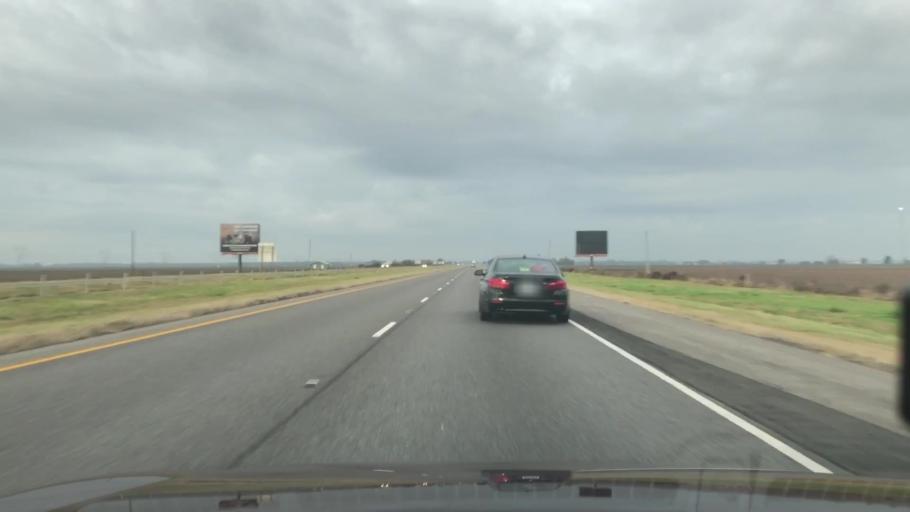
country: US
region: Mississippi
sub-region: Warren County
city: Vicksburg
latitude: 32.3217
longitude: -90.9697
